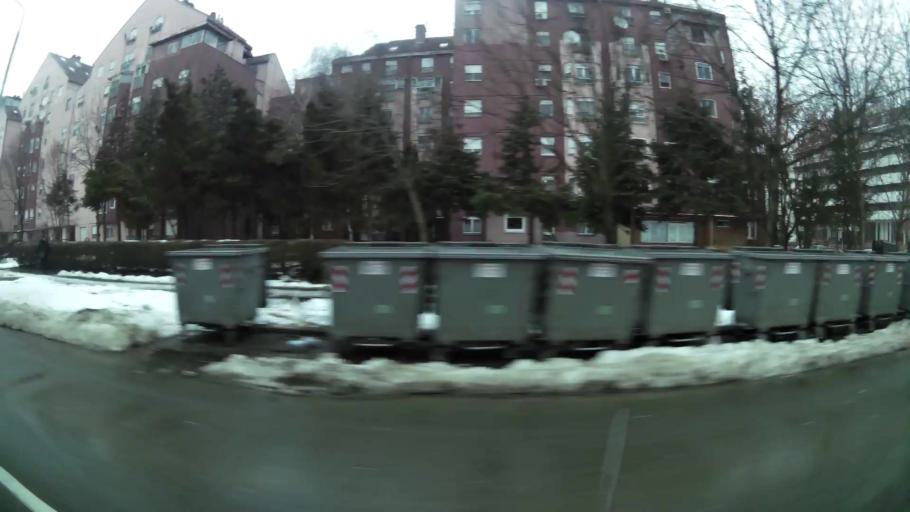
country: RS
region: Central Serbia
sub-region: Belgrade
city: Zemun
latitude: 44.8144
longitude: 20.3757
